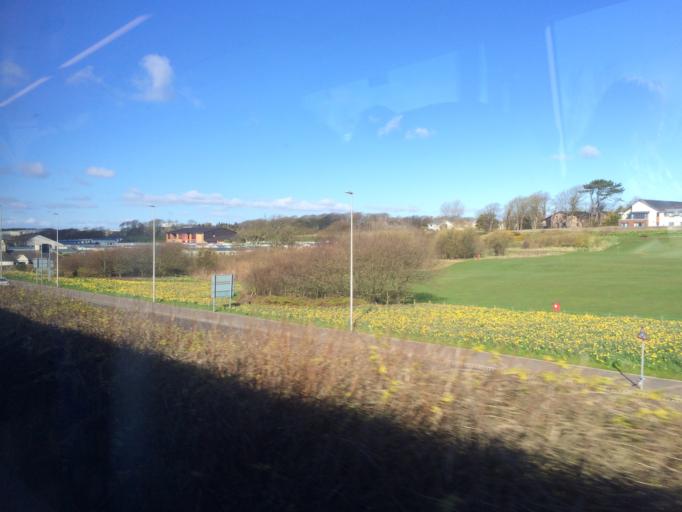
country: GB
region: Scotland
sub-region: Angus
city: Arbroath
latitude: 56.5528
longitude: -2.5994
